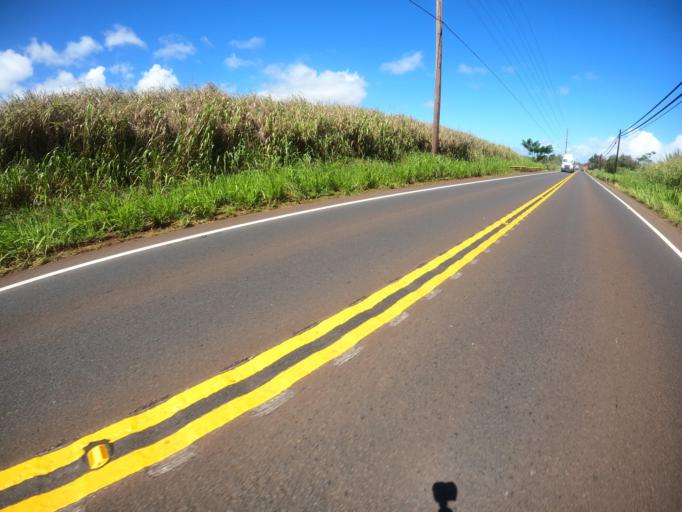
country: US
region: Hawaii
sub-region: Honolulu County
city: Schofield Barracks
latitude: 21.4650
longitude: -158.0551
